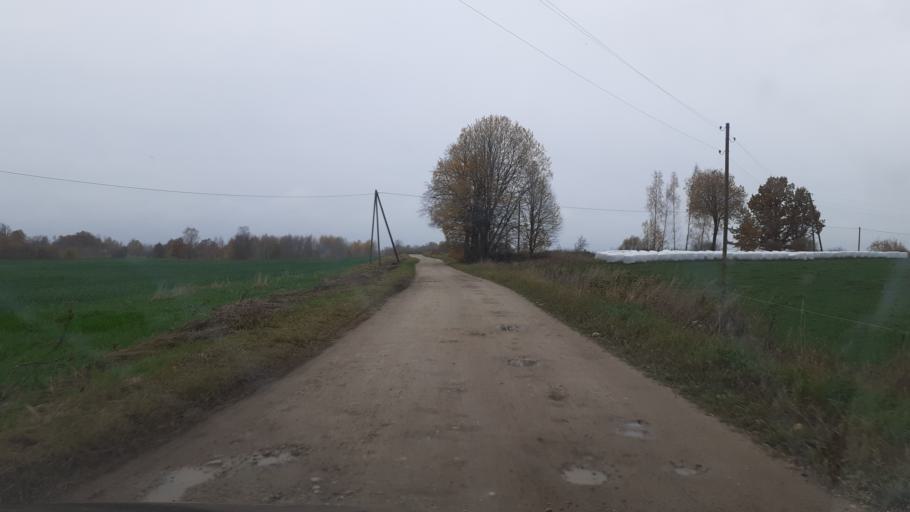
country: LV
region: Saldus Rajons
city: Saldus
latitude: 56.8650
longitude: 22.3476
